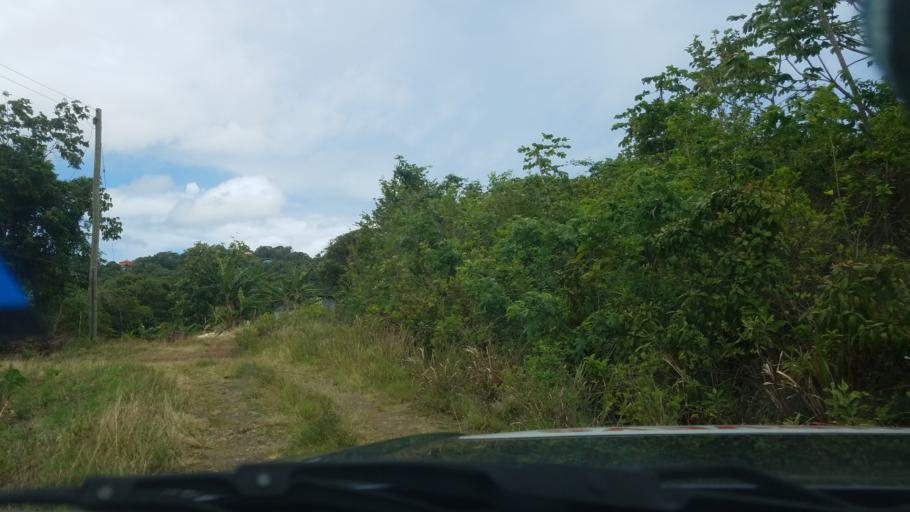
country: LC
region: Castries Quarter
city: Bisee
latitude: 14.0154
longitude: -60.9303
